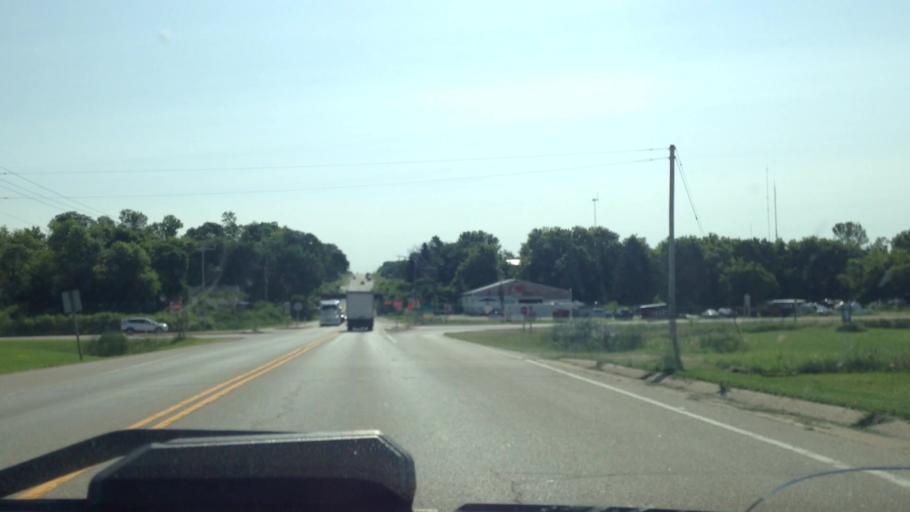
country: US
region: Wisconsin
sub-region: Dodge County
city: Mayville
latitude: 43.4428
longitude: -88.5454
